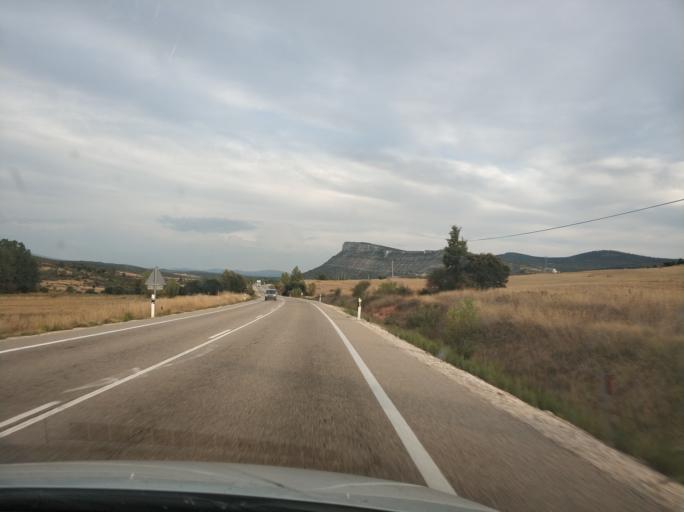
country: ES
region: Castille and Leon
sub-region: Provincia de Burgos
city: Hortiguela
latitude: 42.0759
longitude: -3.4353
